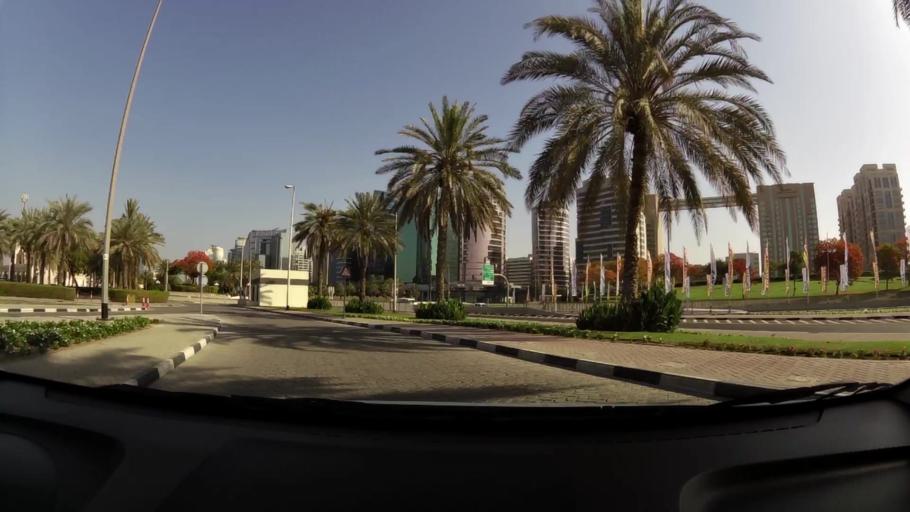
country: AE
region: Ash Shariqah
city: Sharjah
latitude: 25.2556
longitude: 55.3228
